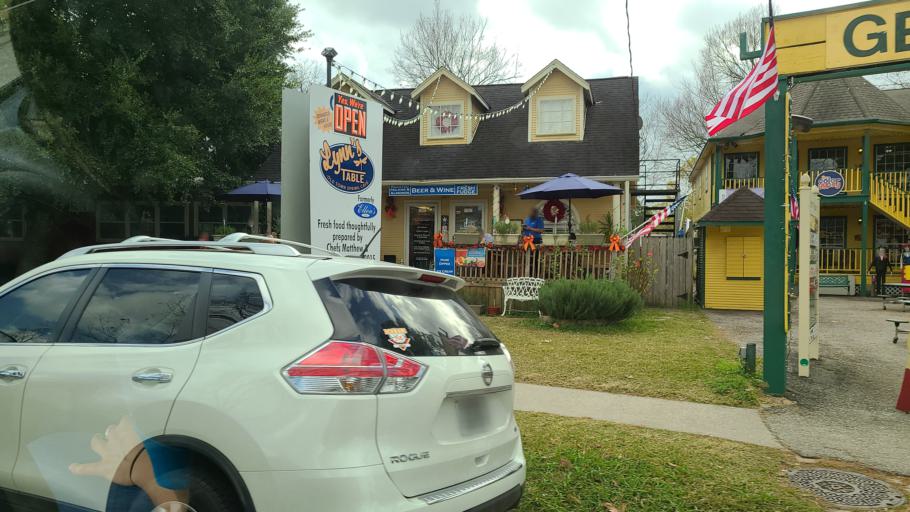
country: US
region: Texas
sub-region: Harris County
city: Spring
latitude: 30.0786
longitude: -95.4198
